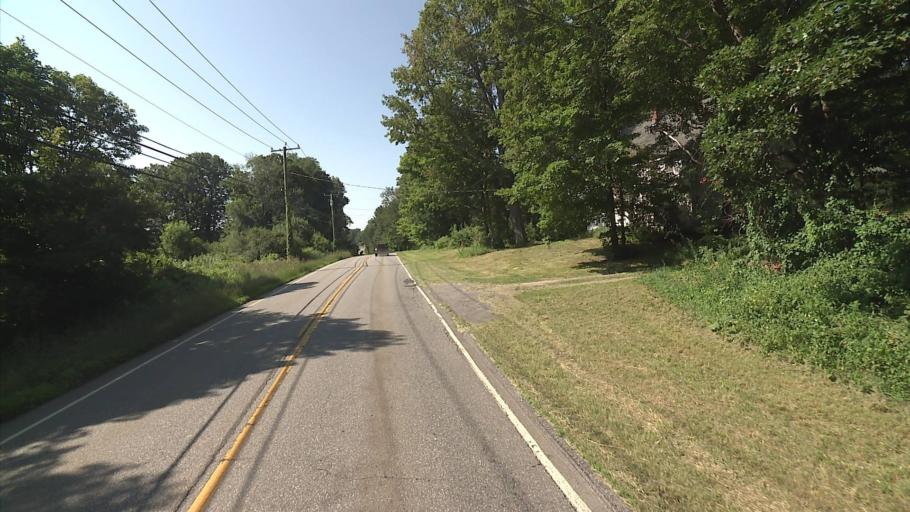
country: US
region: Connecticut
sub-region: Litchfield County
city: Torrington
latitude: 41.8464
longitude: -73.0743
